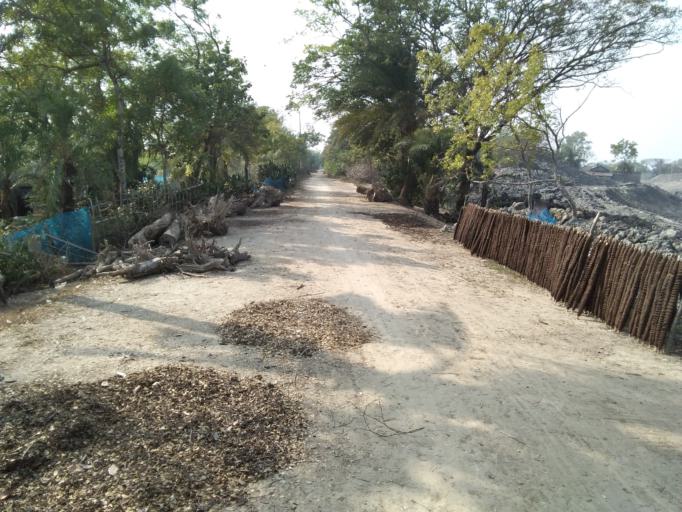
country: IN
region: West Bengal
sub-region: North 24 Parganas
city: Taki
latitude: 22.5906
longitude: 89.0353
